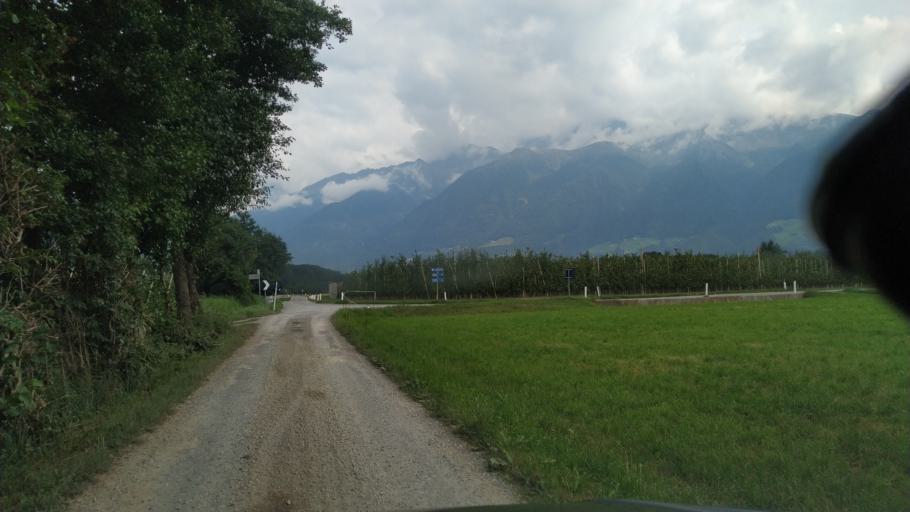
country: IT
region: Trentino-Alto Adige
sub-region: Bolzano
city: Sluderno
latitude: 46.6564
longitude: 10.5752
